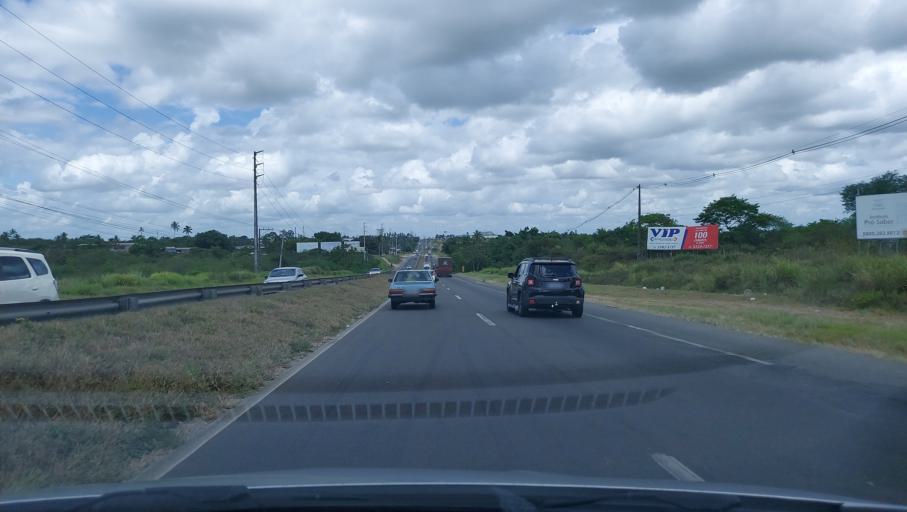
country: BR
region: Bahia
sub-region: Conceicao Do Jacuipe
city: Conceicao do Jacuipe
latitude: -12.3288
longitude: -38.8607
